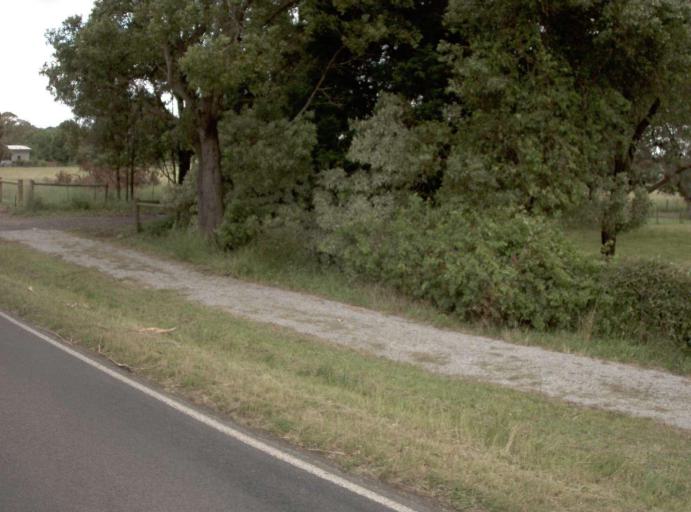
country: AU
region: Victoria
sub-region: Baw Baw
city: Warragul
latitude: -38.1654
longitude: 145.9744
